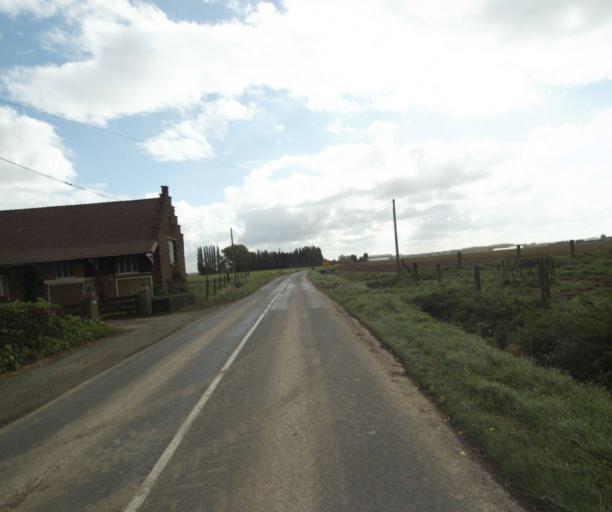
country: FR
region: Nord-Pas-de-Calais
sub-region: Departement du Nord
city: Houplines
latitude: 50.6957
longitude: 2.9355
